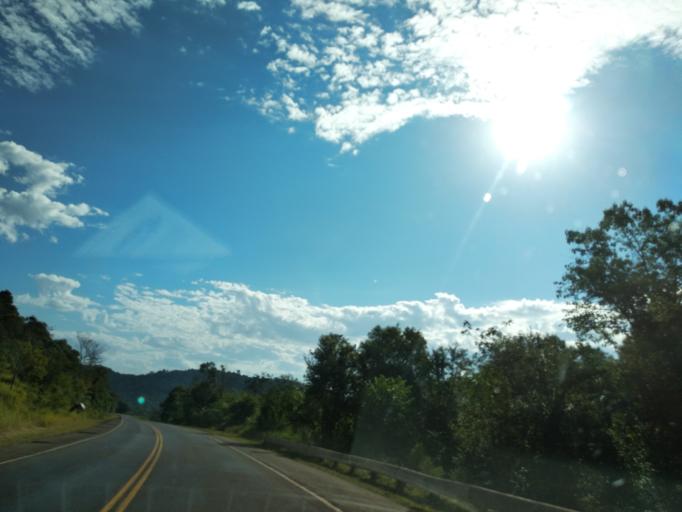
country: AR
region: Misiones
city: Aristobulo del Valle
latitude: -27.0925
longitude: -54.9435
